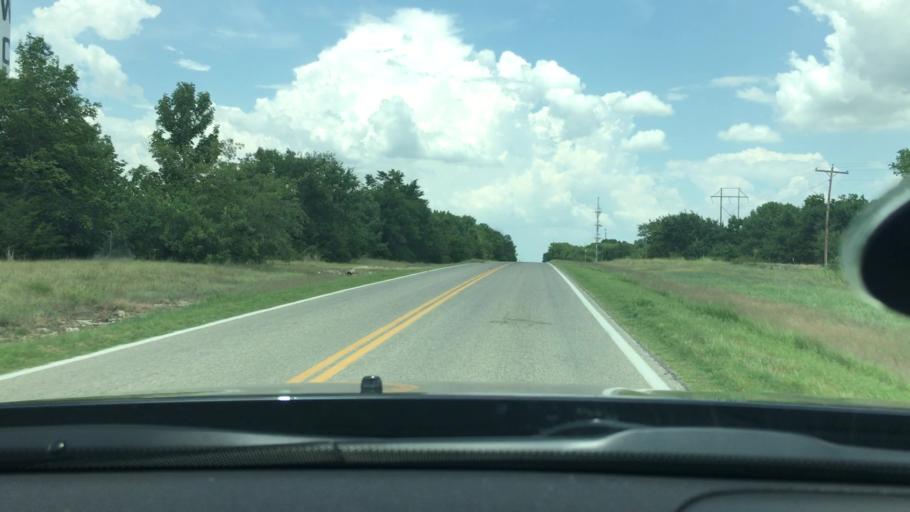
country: US
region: Oklahoma
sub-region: Marshall County
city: Oakland
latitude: 34.0051
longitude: -96.8800
